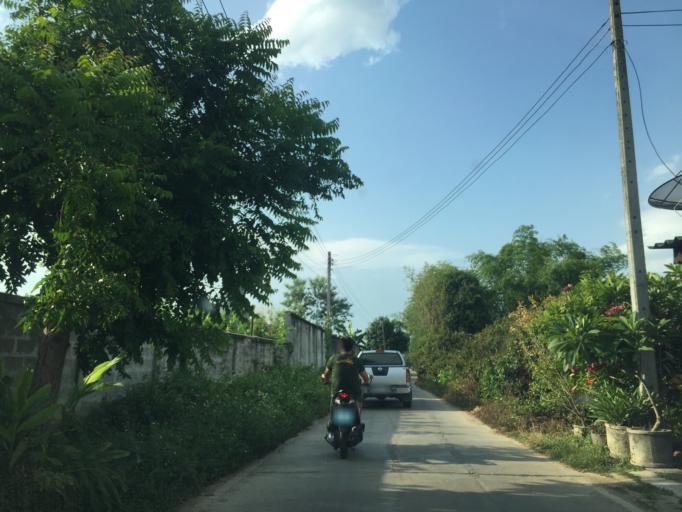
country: TH
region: Lamphun
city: Ban Thi
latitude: 18.6397
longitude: 99.0543
